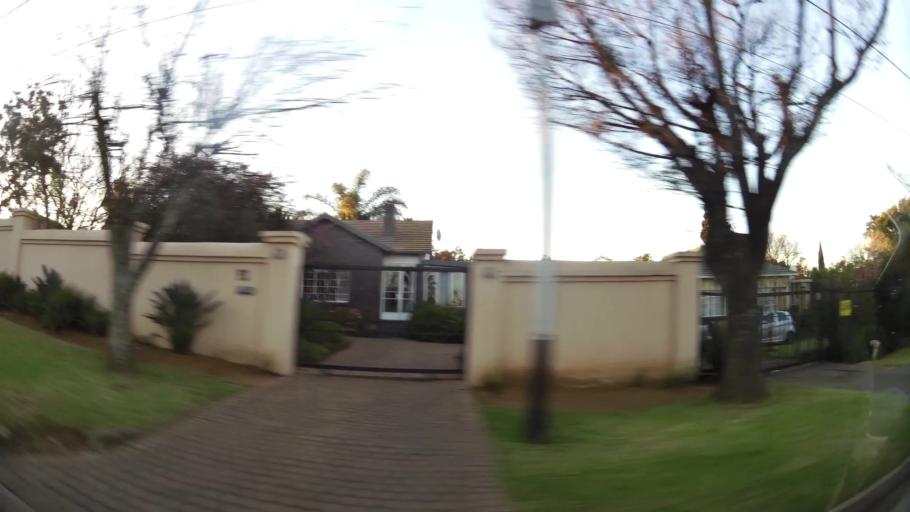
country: ZA
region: Gauteng
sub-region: City of Johannesburg Metropolitan Municipality
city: Roodepoort
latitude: -26.1543
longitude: 27.8838
